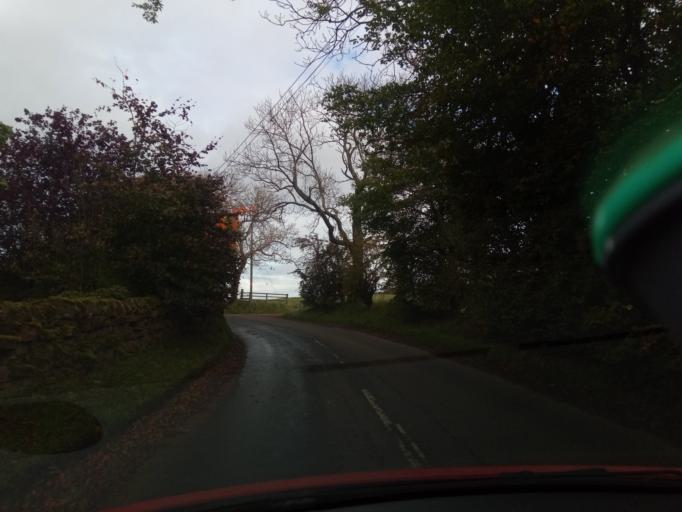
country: GB
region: Scotland
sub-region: South Lanarkshire
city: Carnwath
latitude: 55.7584
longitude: -3.6048
